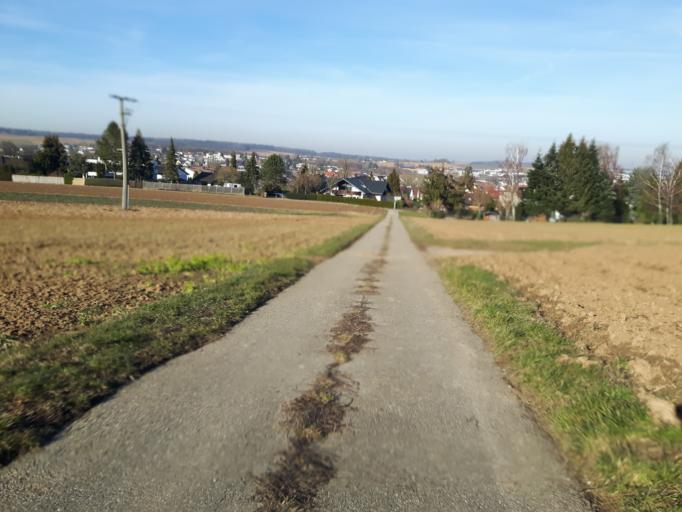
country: DE
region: Baden-Wuerttemberg
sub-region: Regierungsbezirk Stuttgart
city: Leingarten
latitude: 49.1383
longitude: 9.1141
